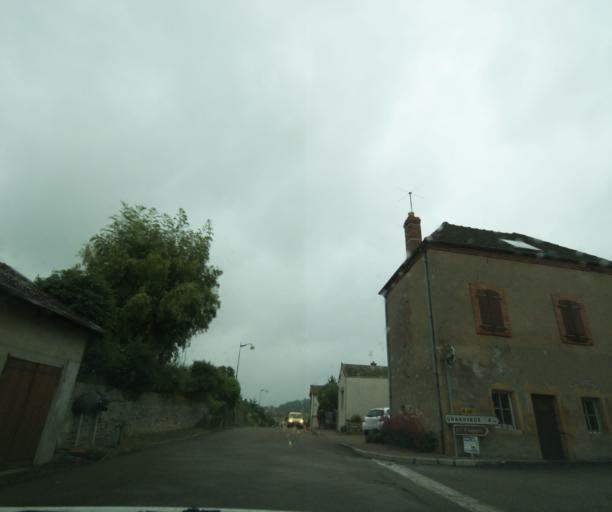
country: FR
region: Bourgogne
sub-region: Departement de Saone-et-Loire
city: Palinges
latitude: 46.4946
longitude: 4.2154
